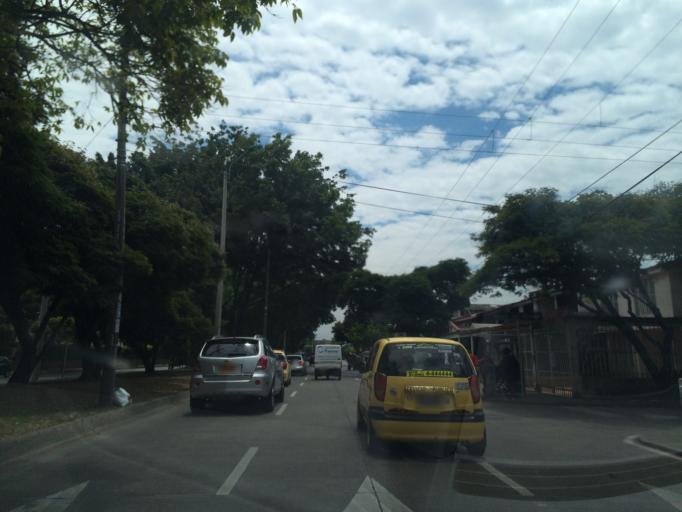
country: CO
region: Valle del Cauca
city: Cali
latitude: 3.4003
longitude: -76.5275
